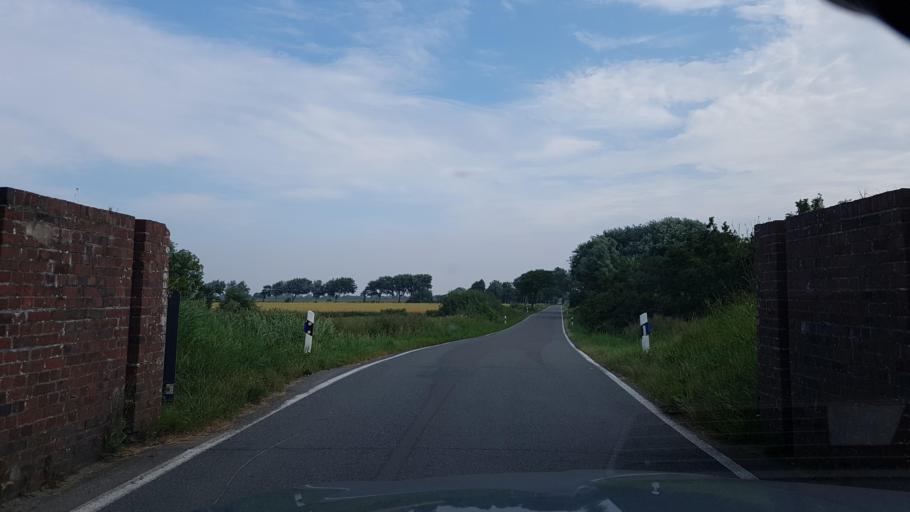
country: DE
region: Schleswig-Holstein
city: Tumlauer Koog
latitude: 54.3654
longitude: 8.7047
